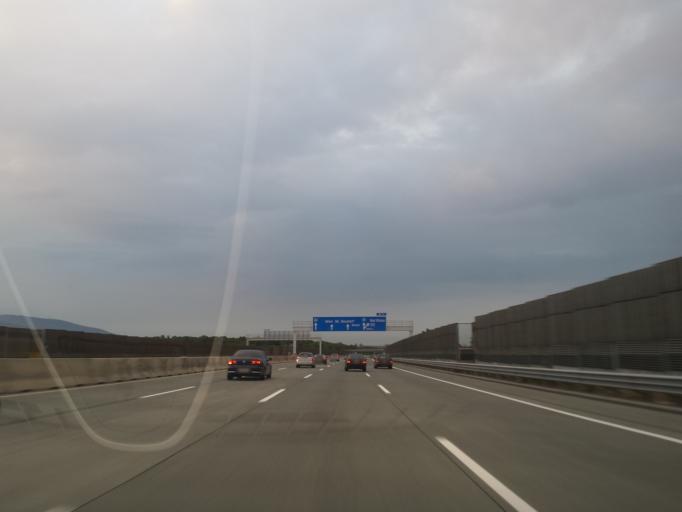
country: AT
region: Lower Austria
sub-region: Politischer Bezirk Baden
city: Kottingbrunn
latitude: 47.9617
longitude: 16.2268
